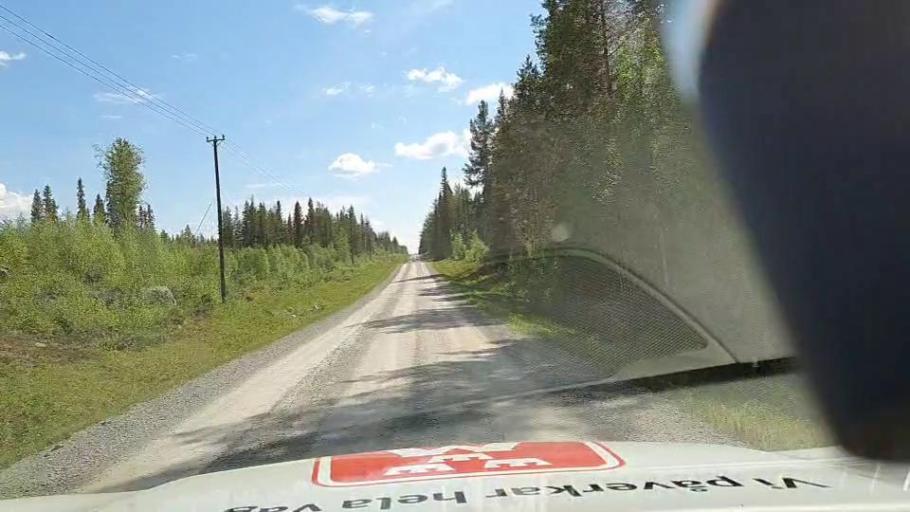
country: SE
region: Jaemtland
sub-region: Stroemsunds Kommun
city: Stroemsund
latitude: 64.4844
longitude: 15.5918
